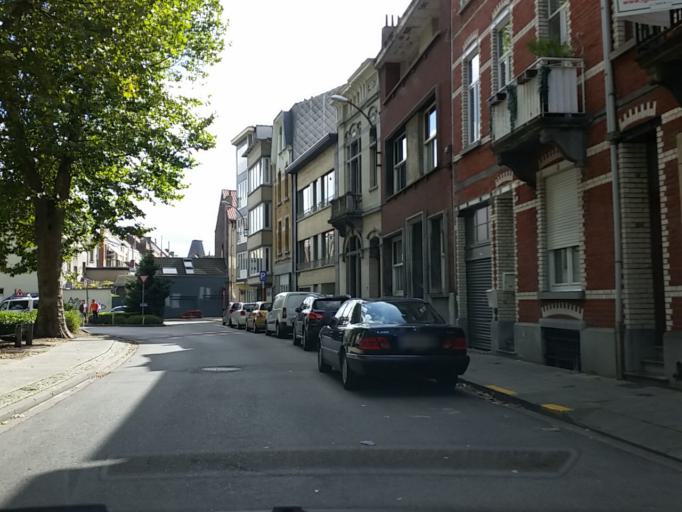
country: BE
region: Flanders
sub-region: Provincie Vlaams-Brabant
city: Vilvoorde
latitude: 50.9292
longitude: 4.4298
